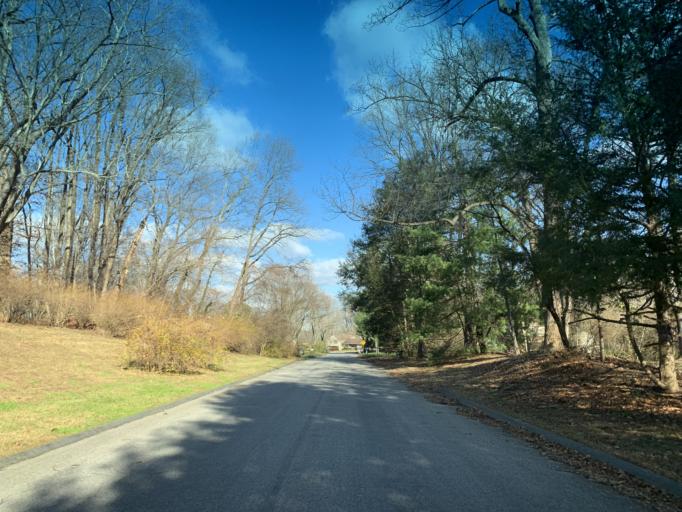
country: US
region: Maryland
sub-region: Harford County
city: South Bel Air
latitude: 39.5778
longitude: -76.2447
